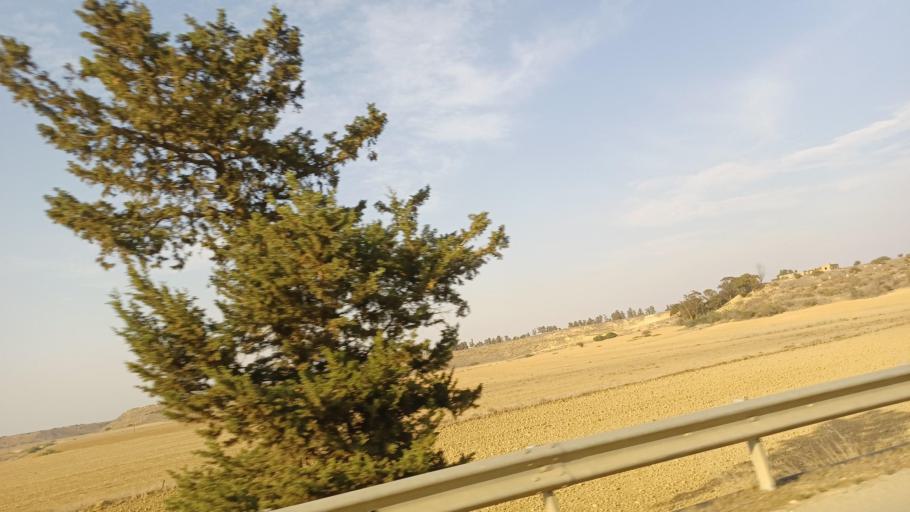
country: CY
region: Ammochostos
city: Avgorou
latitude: 35.0663
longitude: 33.8513
